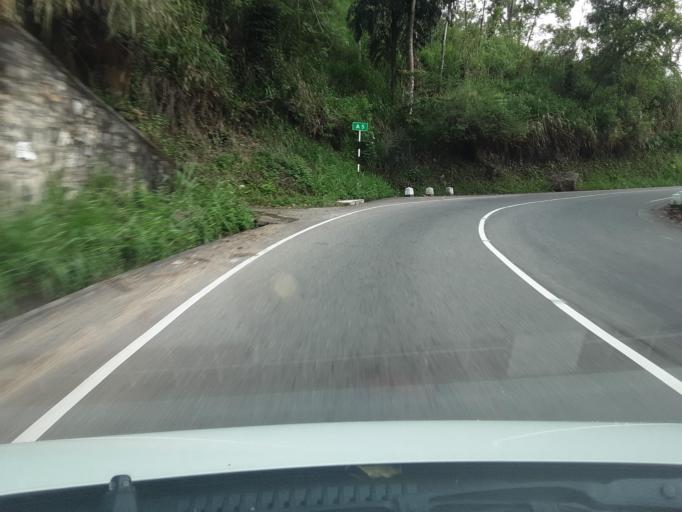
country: LK
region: Uva
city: Badulla
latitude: 6.9414
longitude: 81.0169
